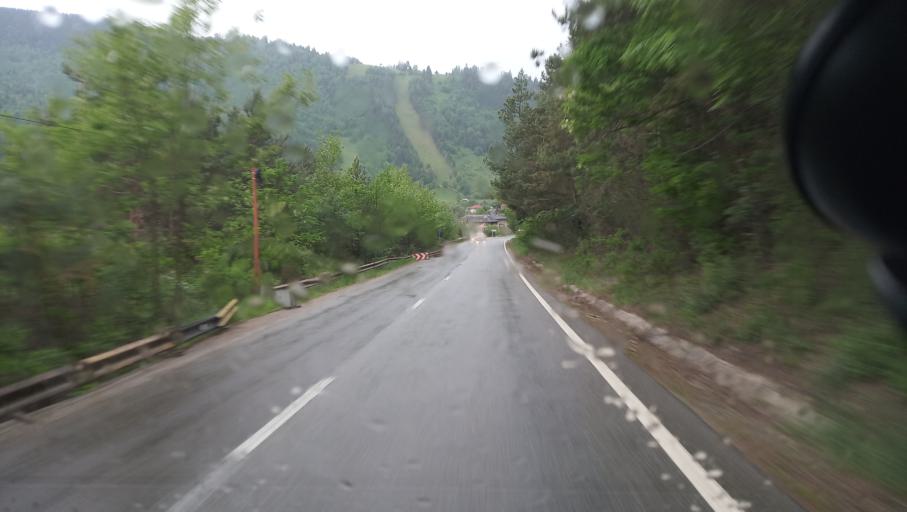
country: RO
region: Neamt
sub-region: Comuna Ceahlau
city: Ceahlau
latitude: 47.0582
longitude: 25.9229
